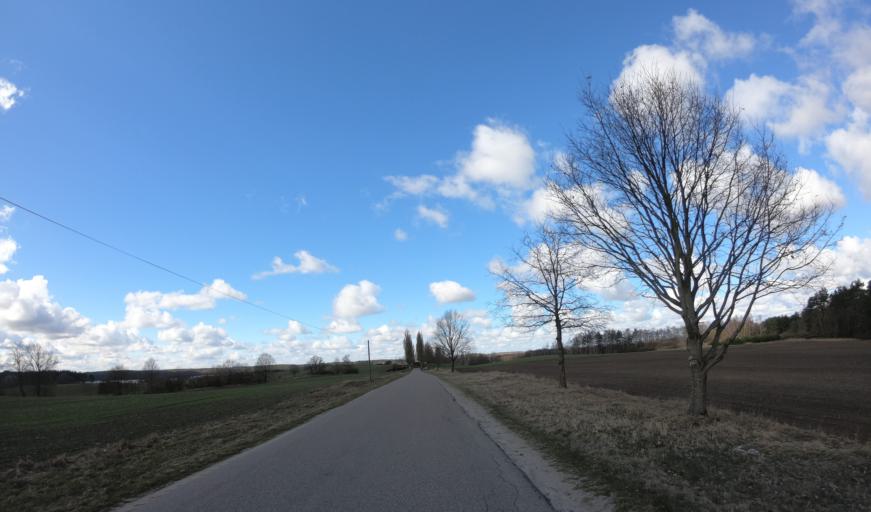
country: PL
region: West Pomeranian Voivodeship
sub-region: Powiat drawski
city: Drawsko Pomorskie
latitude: 53.4841
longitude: 15.8837
